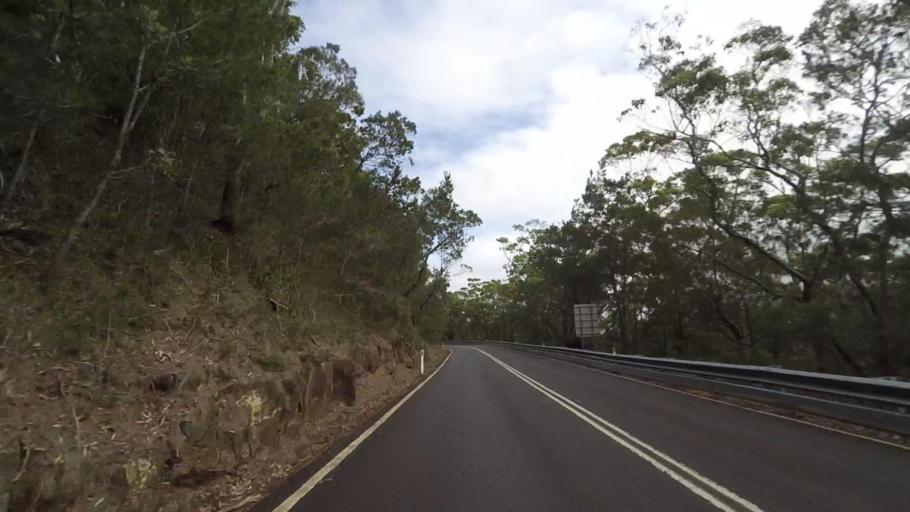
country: AU
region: New South Wales
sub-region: Wollongong
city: Helensburgh
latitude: -34.2180
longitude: 150.9991
